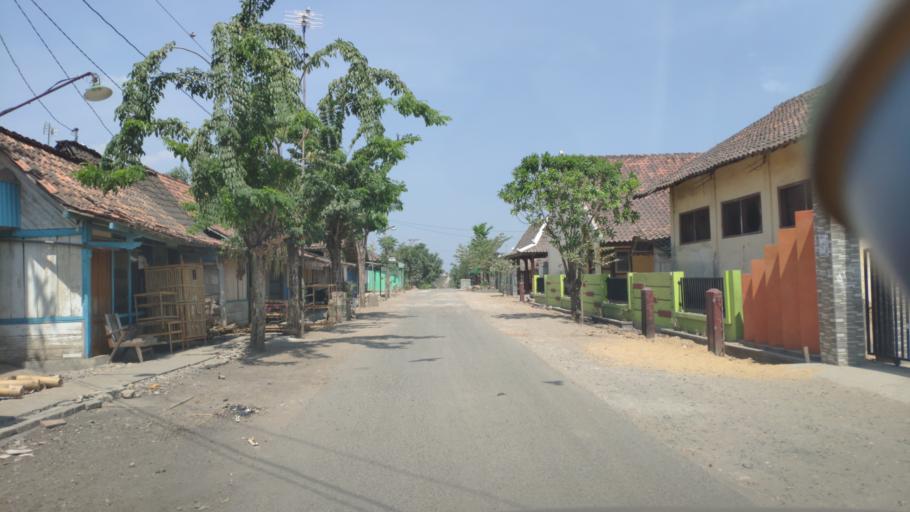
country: ID
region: Central Java
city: Pipes
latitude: -7.1032
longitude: 111.2486
